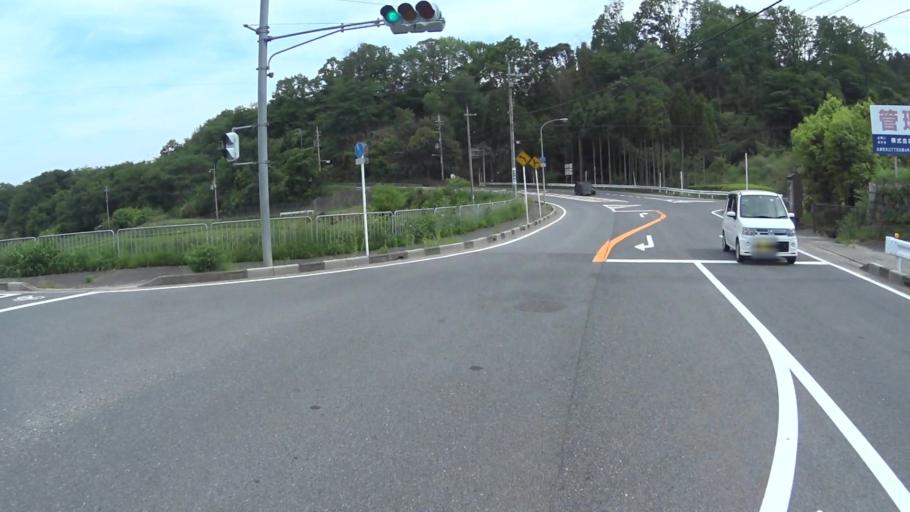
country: JP
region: Shiga Prefecture
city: Kitahama
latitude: 35.1579
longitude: 135.8697
